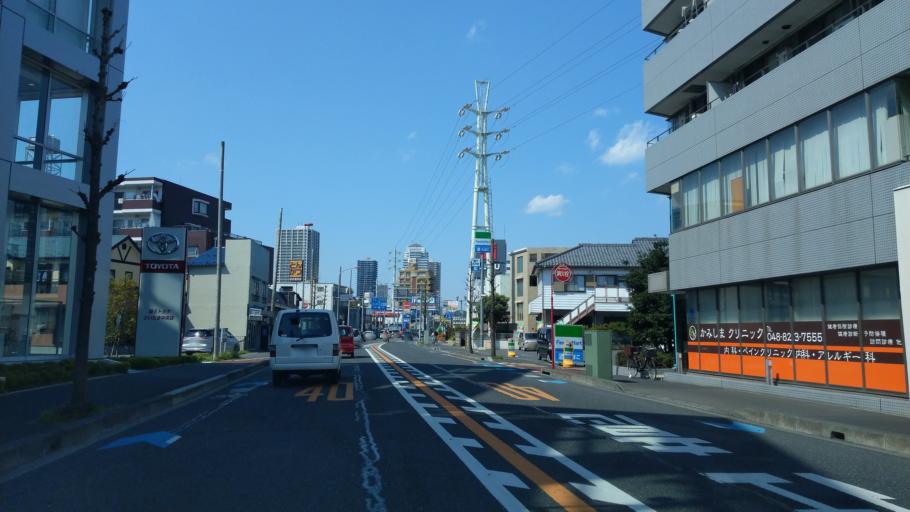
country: JP
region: Saitama
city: Yono
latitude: 35.8828
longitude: 139.6323
